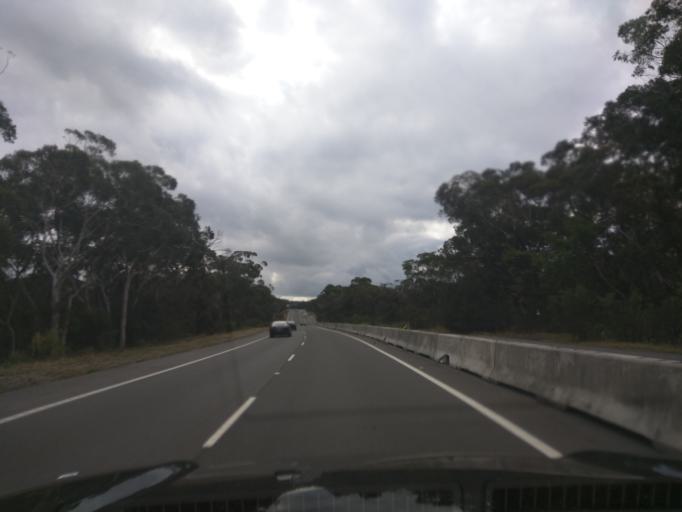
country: AU
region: New South Wales
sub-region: Wollongong
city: Mount Keira
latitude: -34.3701
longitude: 150.8280
